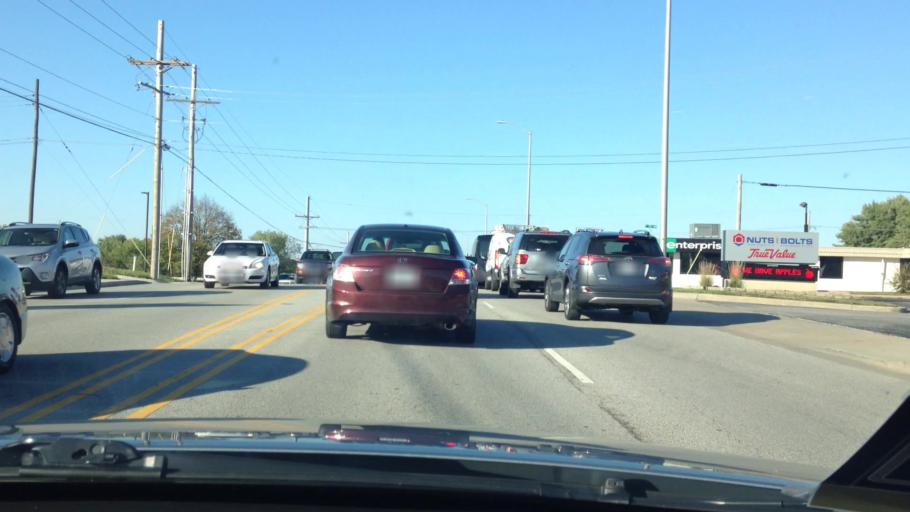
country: US
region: Missouri
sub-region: Clay County
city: Gladstone
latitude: 39.2305
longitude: -94.5761
